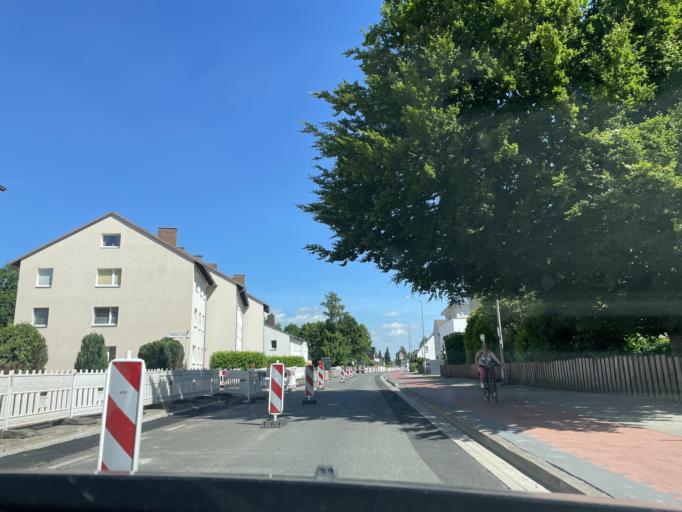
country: DE
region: North Rhine-Westphalia
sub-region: Regierungsbezirk Detmold
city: Minden
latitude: 52.3056
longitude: 8.9113
